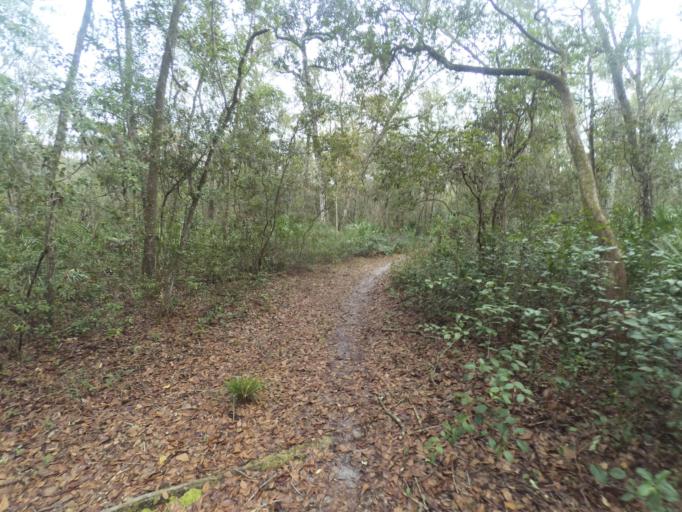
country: US
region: Florida
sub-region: Alachua County
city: Gainesville
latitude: 29.5442
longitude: -82.2789
